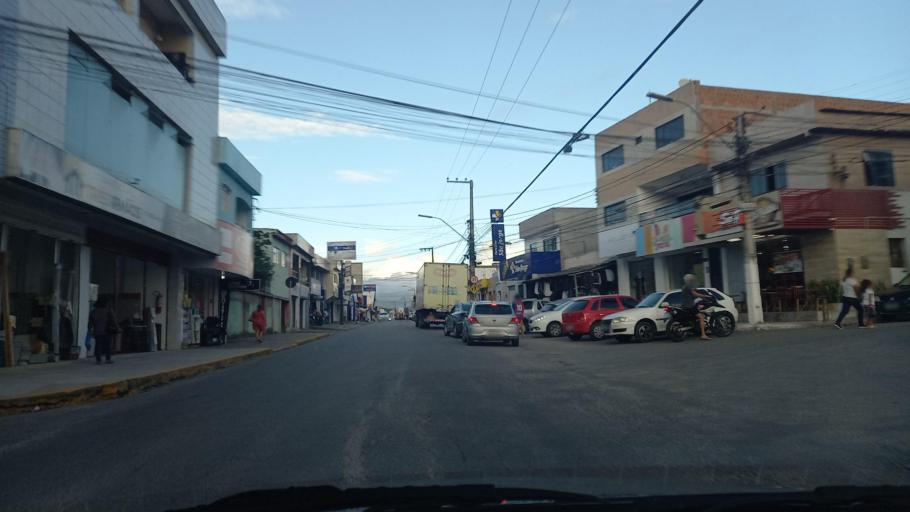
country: BR
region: Pernambuco
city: Garanhuns
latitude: -8.8845
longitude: -36.4699
